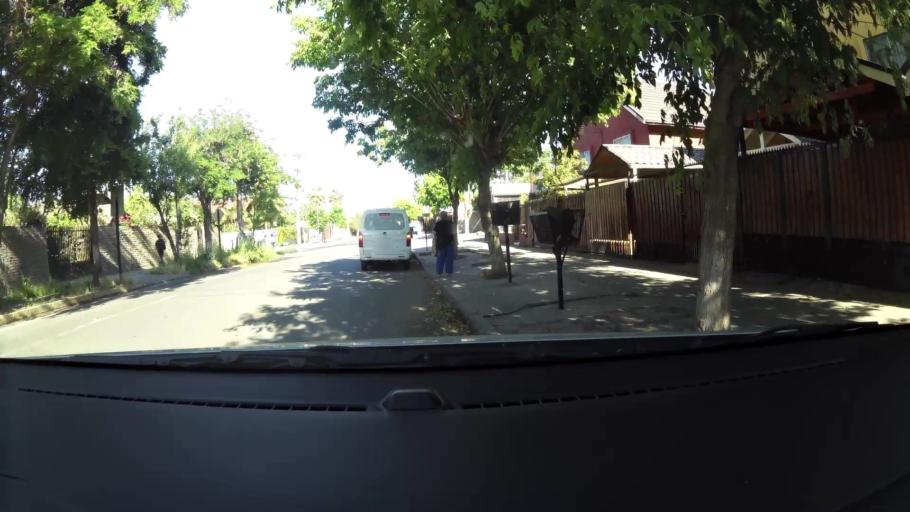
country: CL
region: Santiago Metropolitan
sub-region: Provincia de Maipo
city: San Bernardo
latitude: -33.6183
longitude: -70.6895
